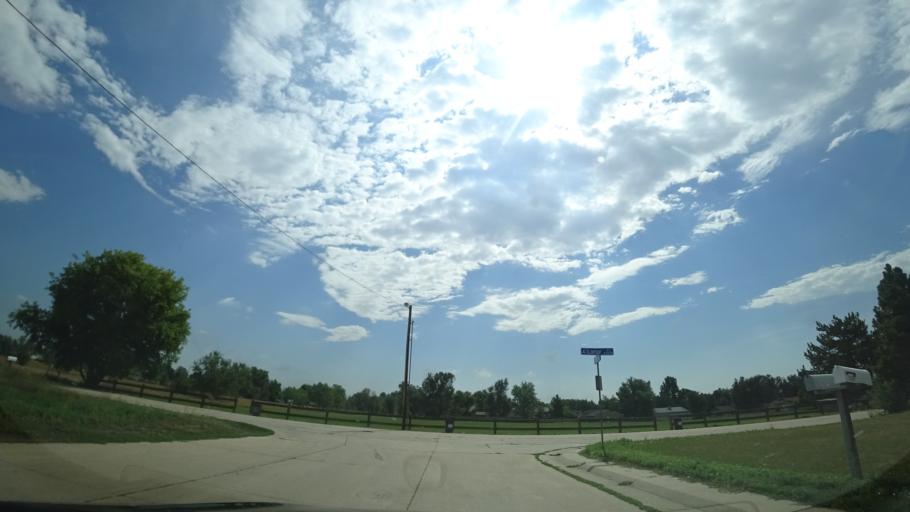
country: US
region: Colorado
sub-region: Jefferson County
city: Lakewood
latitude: 39.7203
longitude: -105.0678
